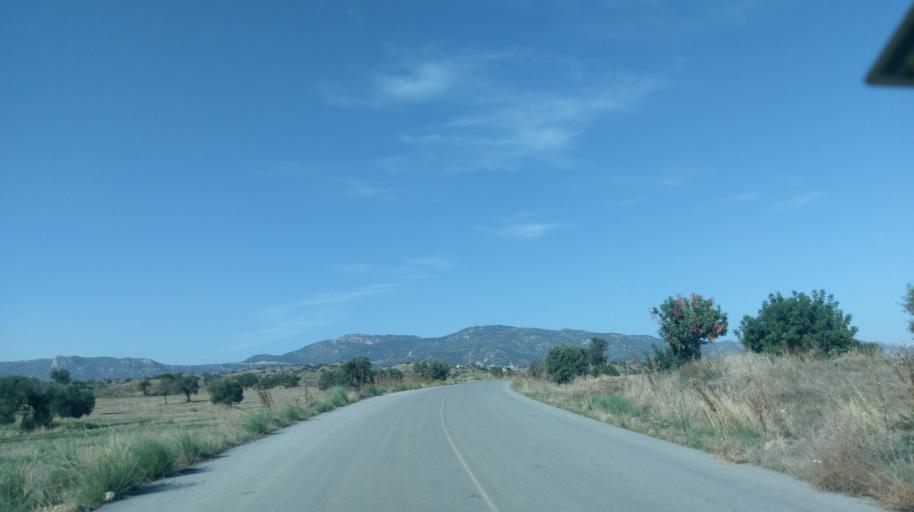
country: CY
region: Ammochostos
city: Trikomo
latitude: 35.3270
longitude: 33.8932
